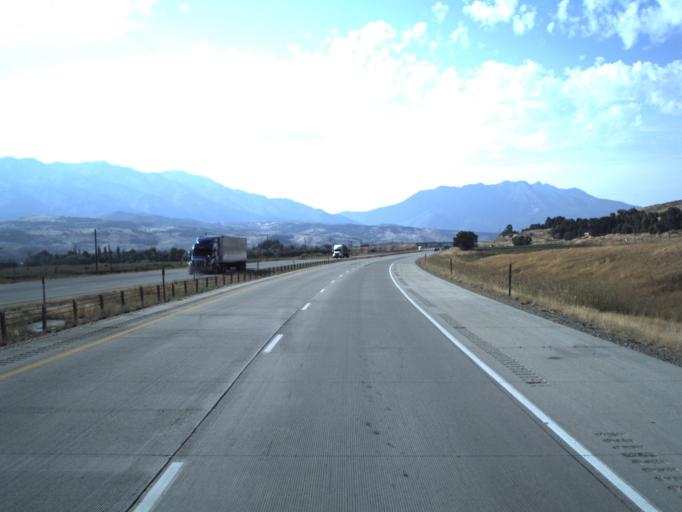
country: US
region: Utah
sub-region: Morgan County
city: Morgan
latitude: 41.0579
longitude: -111.6982
